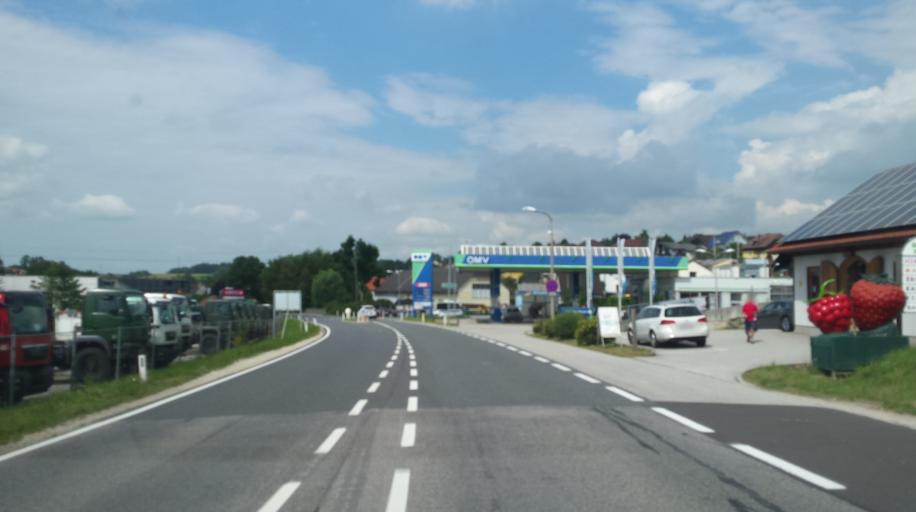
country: AT
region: Lower Austria
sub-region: Politischer Bezirk Amstetten
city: Haag
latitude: 48.1151
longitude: 14.5718
